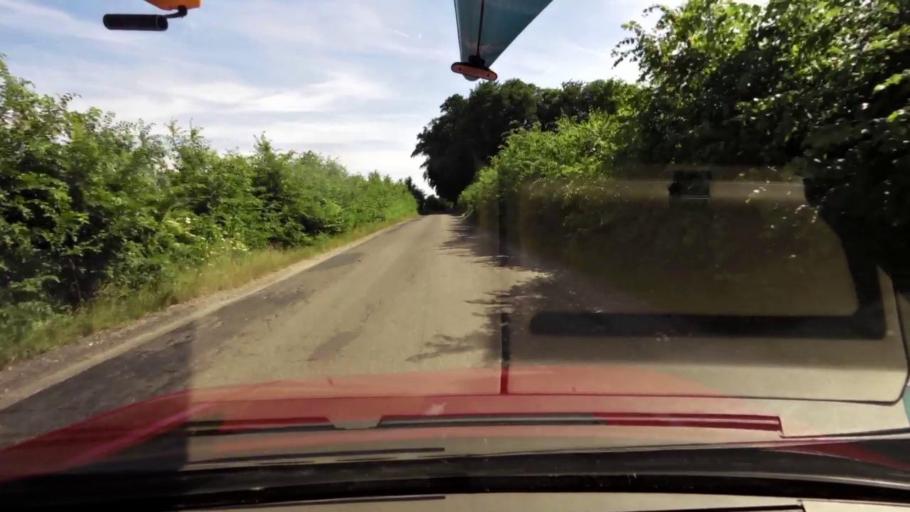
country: PL
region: Pomeranian Voivodeship
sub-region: Powiat slupski
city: Kobylnica
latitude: 54.3707
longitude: 16.9666
